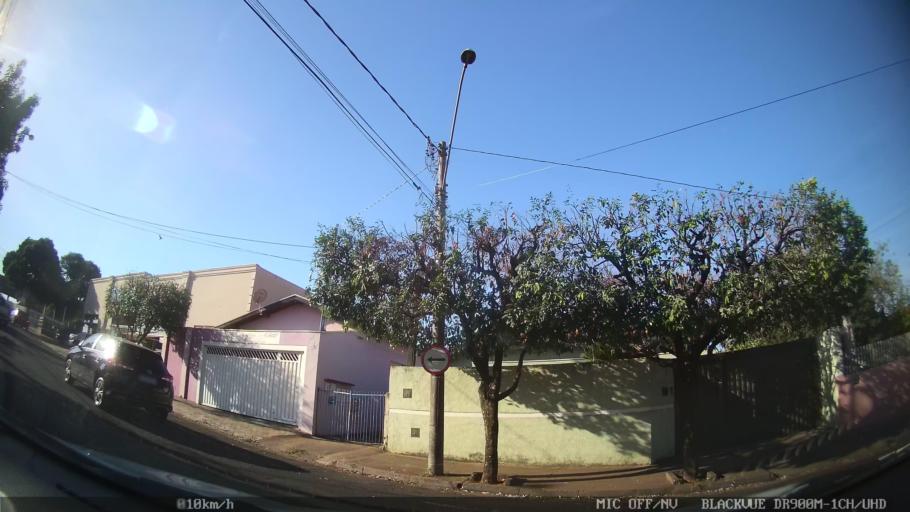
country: BR
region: Sao Paulo
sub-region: Sao Jose Do Rio Preto
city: Sao Jose do Rio Preto
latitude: -20.8125
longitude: -49.3979
